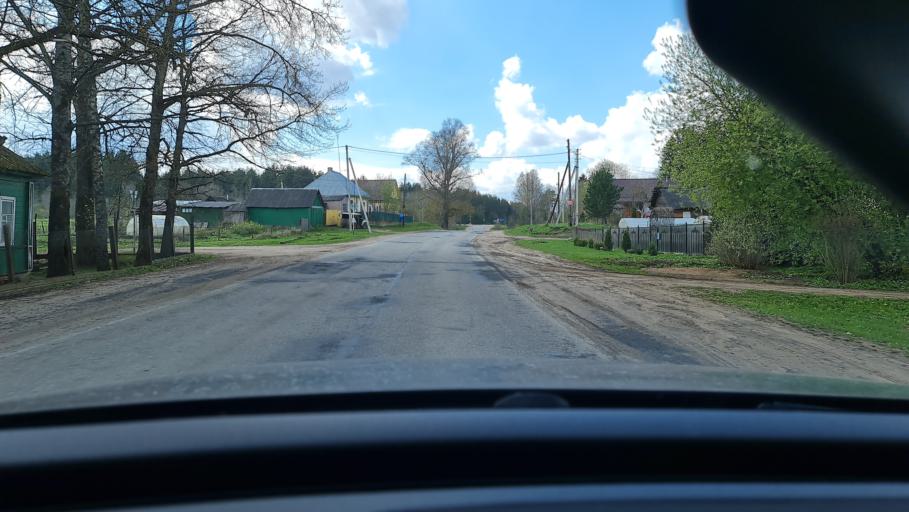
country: RU
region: Tverskaya
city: Toropets
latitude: 56.4222
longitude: 31.6408
